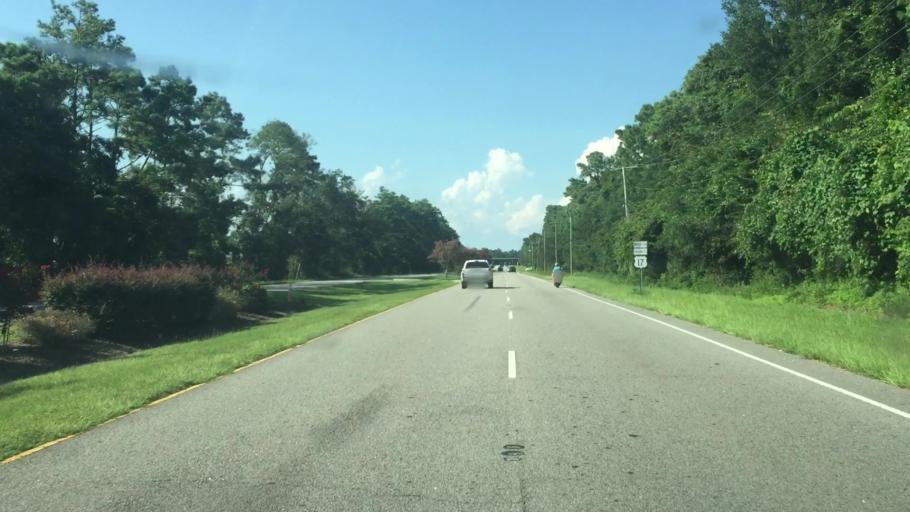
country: US
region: South Carolina
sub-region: Horry County
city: Myrtle Beach
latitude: 33.7592
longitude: -78.8067
